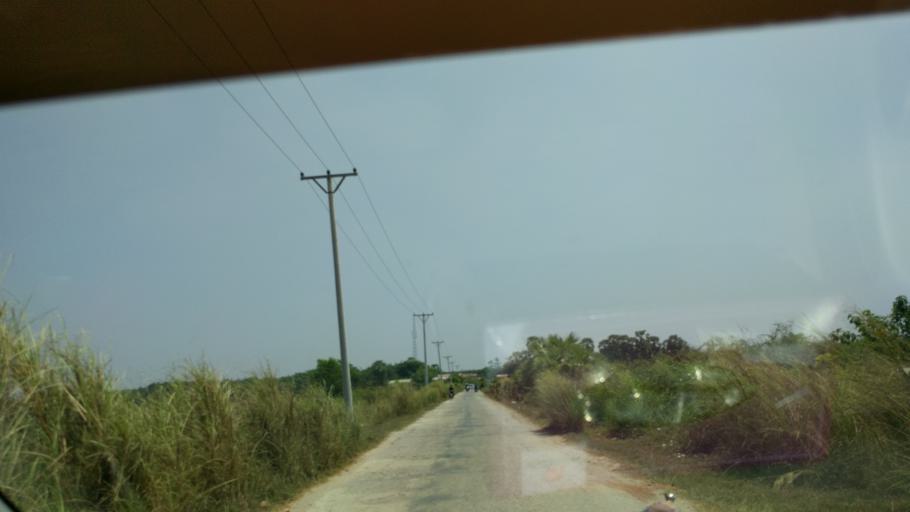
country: MM
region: Mon
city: Martaban
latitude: 16.5864
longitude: 97.6812
